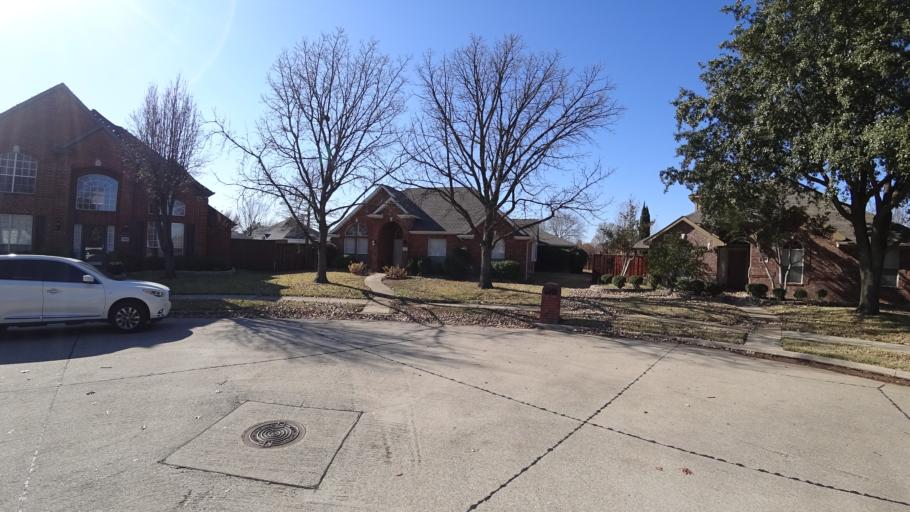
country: US
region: Texas
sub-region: Denton County
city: Lewisville
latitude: 33.0112
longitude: -97.0249
